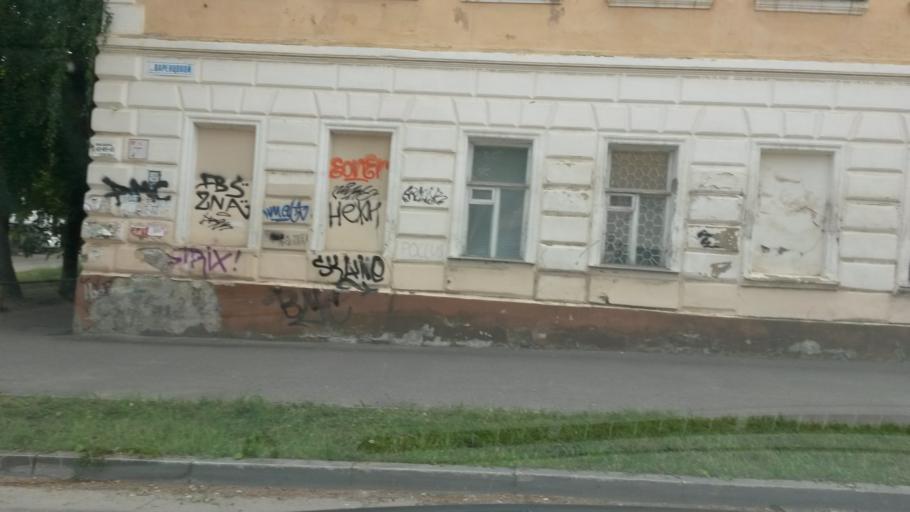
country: RU
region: Ivanovo
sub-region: Gorod Ivanovo
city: Ivanovo
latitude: 56.9923
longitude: 40.9784
